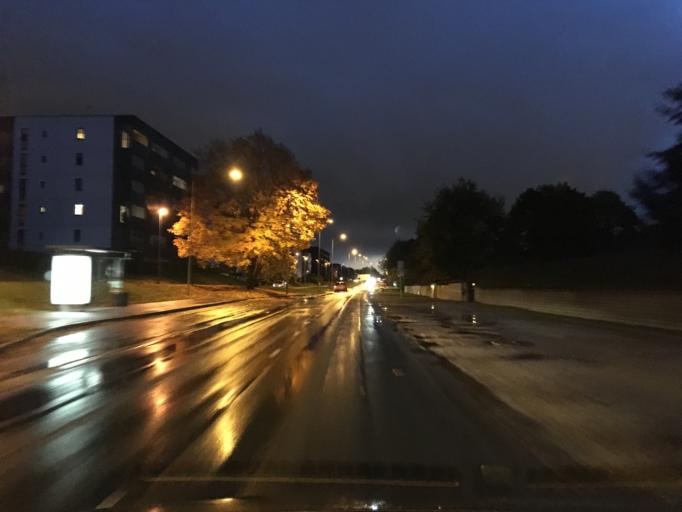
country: EE
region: Harju
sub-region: Tallinna linn
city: Tallinn
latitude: 59.4412
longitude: 24.8087
